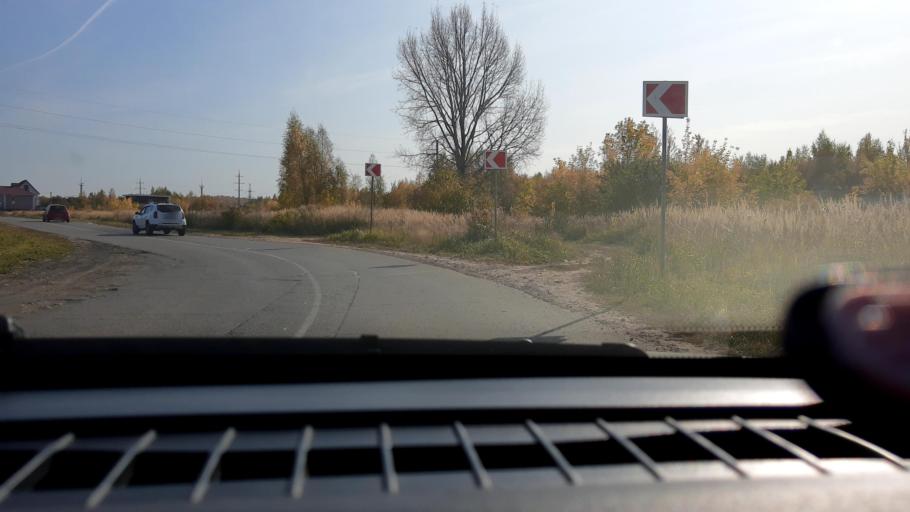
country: RU
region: Nizjnij Novgorod
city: Kstovo
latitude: 56.1479
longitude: 44.2273
